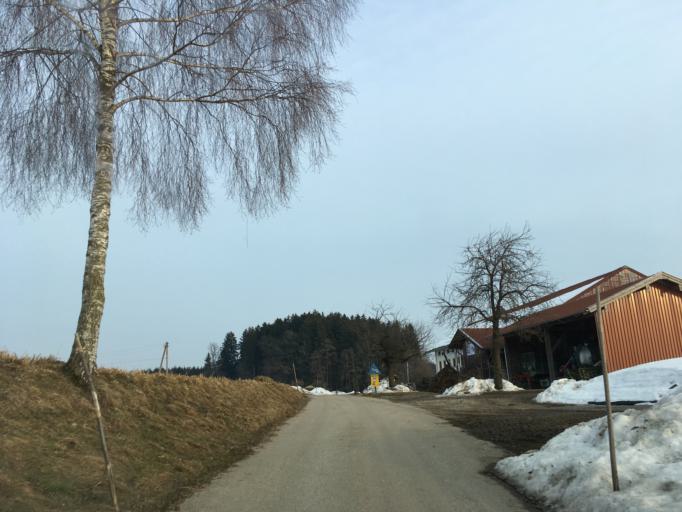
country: DE
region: Bavaria
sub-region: Upper Bavaria
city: Bad Endorf
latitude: 47.9260
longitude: 12.2984
